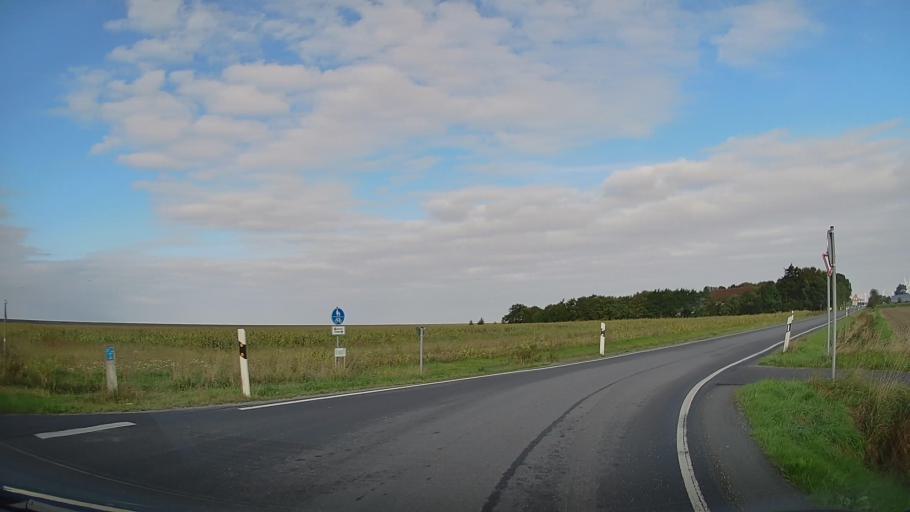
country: DE
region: Schleswig-Holstein
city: Reussenkoge
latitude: 54.5708
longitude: 8.9292
